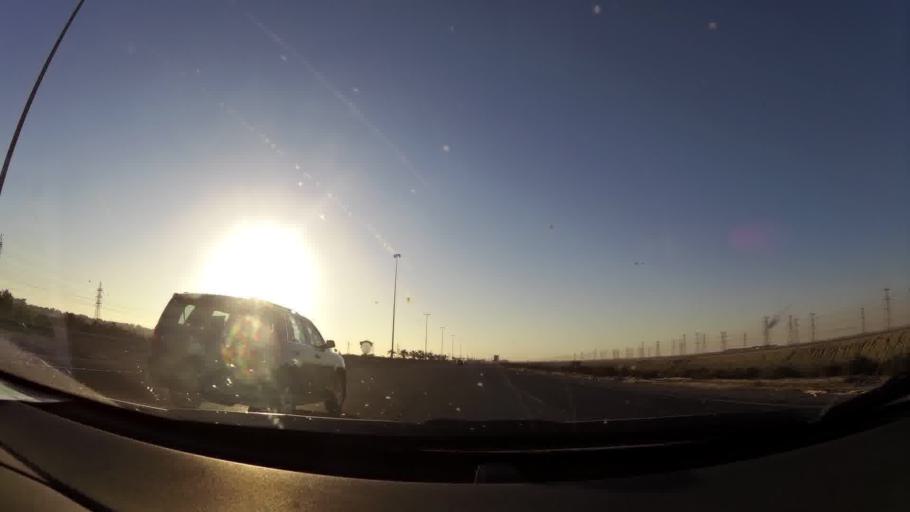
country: KW
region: Al Ahmadi
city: Al Fahahil
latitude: 28.9098
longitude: 48.2135
